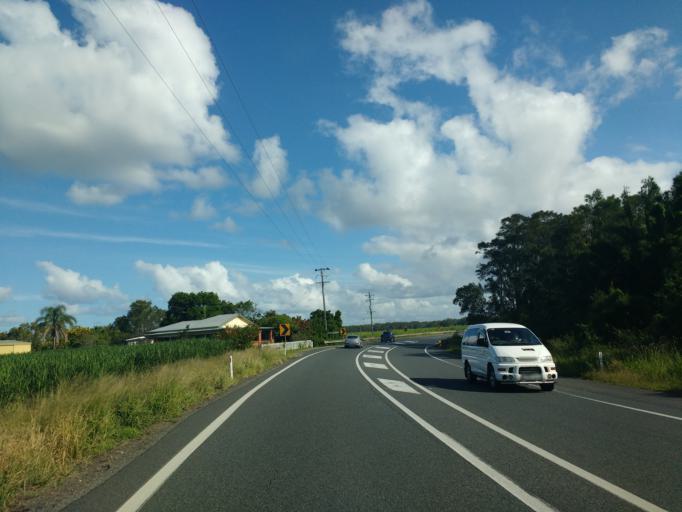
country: AU
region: New South Wales
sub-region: Richmond Valley
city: Evans Head
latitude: -28.9917
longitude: 153.4622
